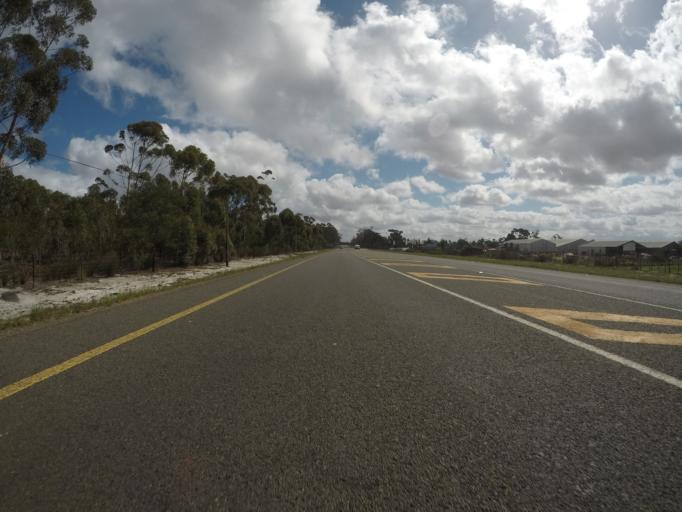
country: ZA
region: Western Cape
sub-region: Eden District Municipality
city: Riversdale
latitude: -34.2128
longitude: 21.5774
